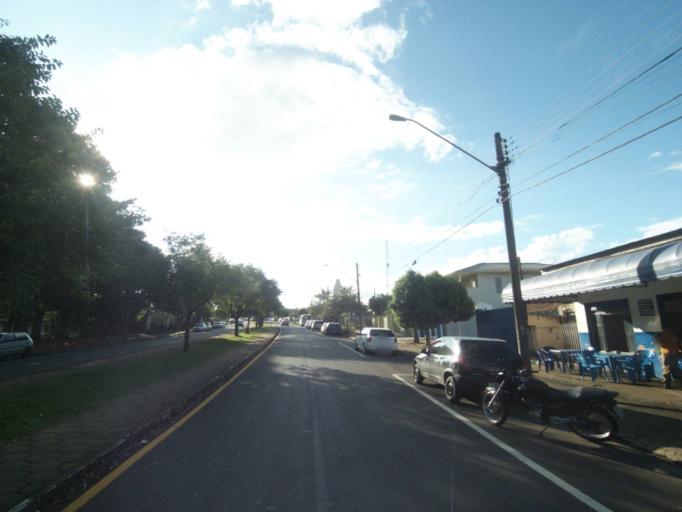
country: BR
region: Parana
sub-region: Telemaco Borba
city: Telemaco Borba
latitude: -24.3302
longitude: -50.6139
